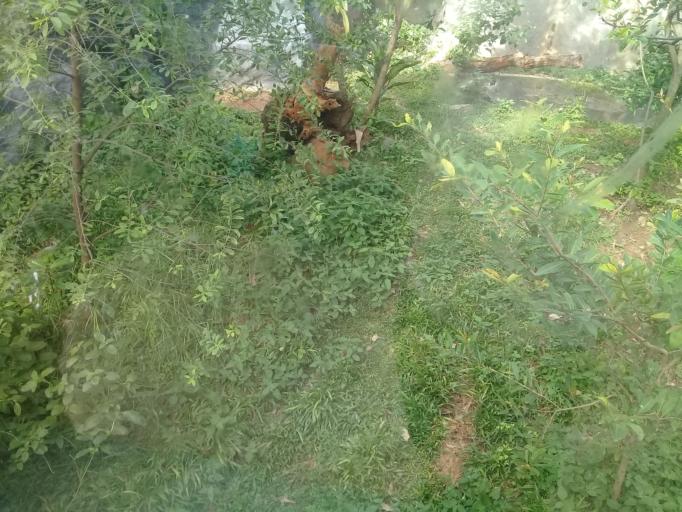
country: LK
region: Western
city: Galkissa
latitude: 6.8571
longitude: 79.8739
